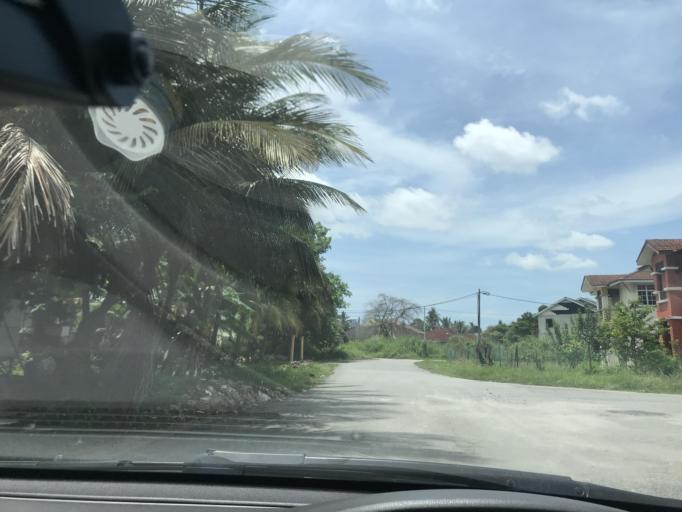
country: MY
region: Kelantan
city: Kota Bharu
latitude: 6.1239
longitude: 102.2194
